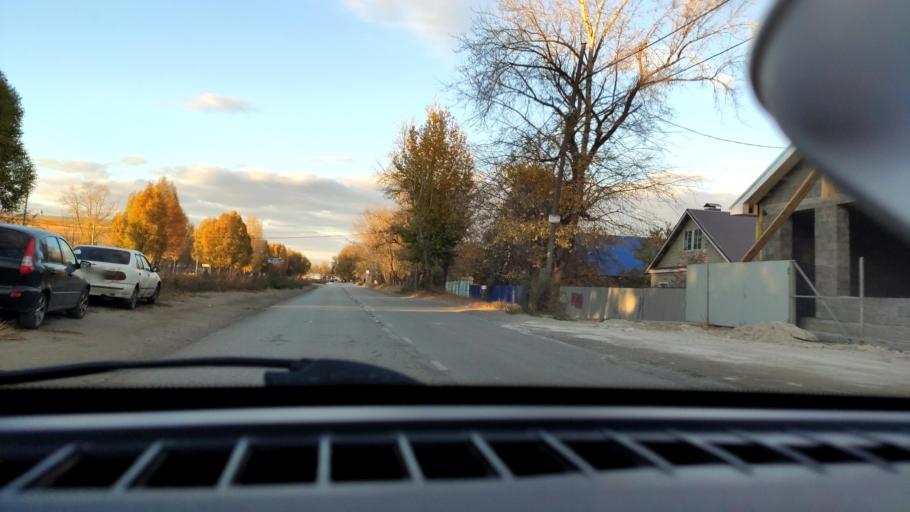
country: RU
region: Samara
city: Petra-Dubrava
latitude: 53.2390
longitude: 50.3081
